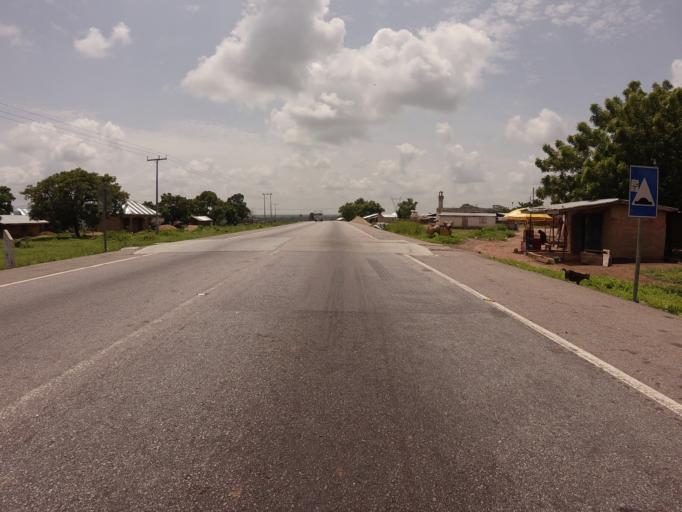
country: GH
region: Northern
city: Tamale
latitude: 9.1296
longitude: -1.1949
